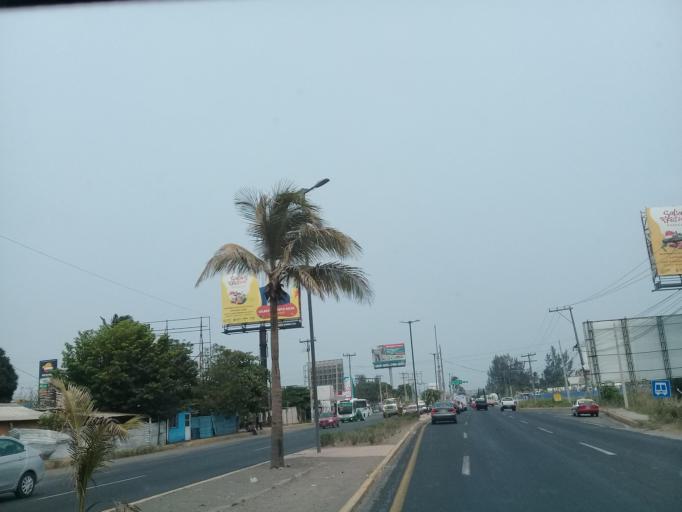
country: MX
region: Veracruz
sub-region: Veracruz
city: Hacienda Sotavento
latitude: 19.1443
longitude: -96.1607
